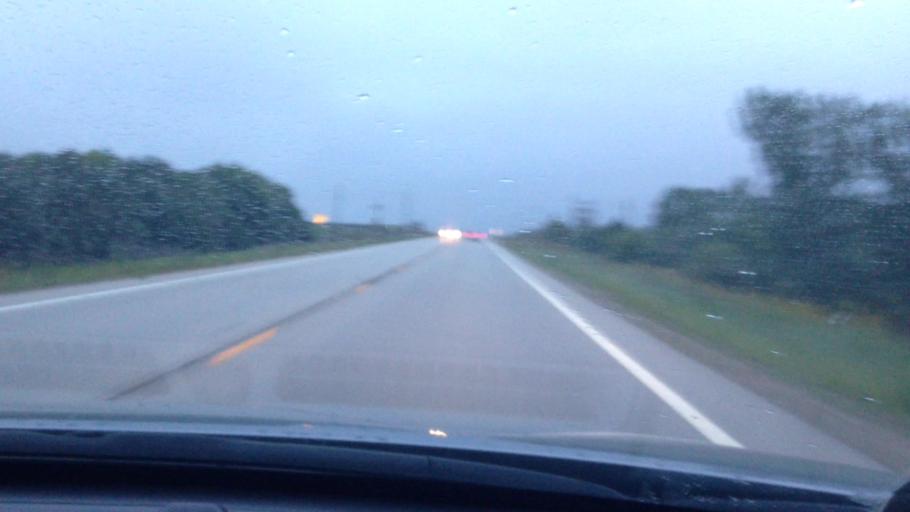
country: US
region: Kansas
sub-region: Brown County
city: Horton
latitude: 39.6675
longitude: -95.4938
